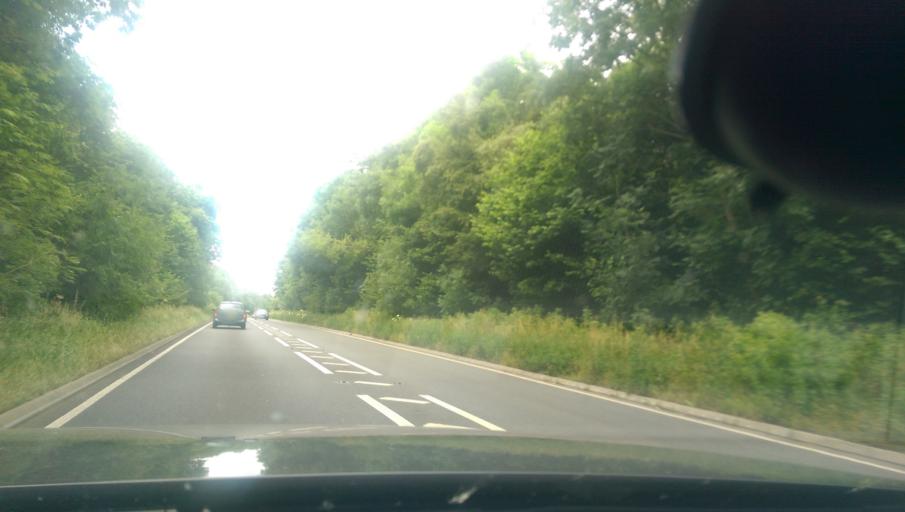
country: GB
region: England
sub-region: Wiltshire
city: Stockton
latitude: 51.1187
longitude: -2.0451
